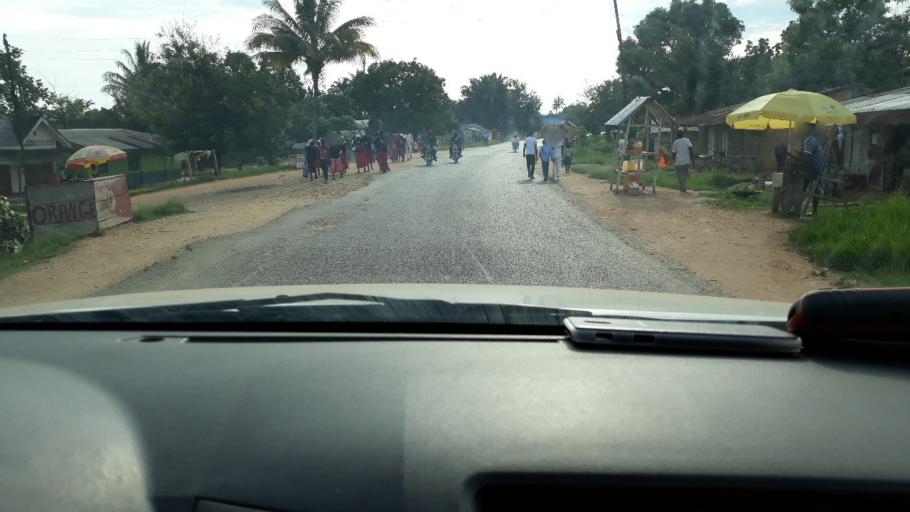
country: CD
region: Maniema
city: Kindu
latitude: -2.9523
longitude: 25.9409
